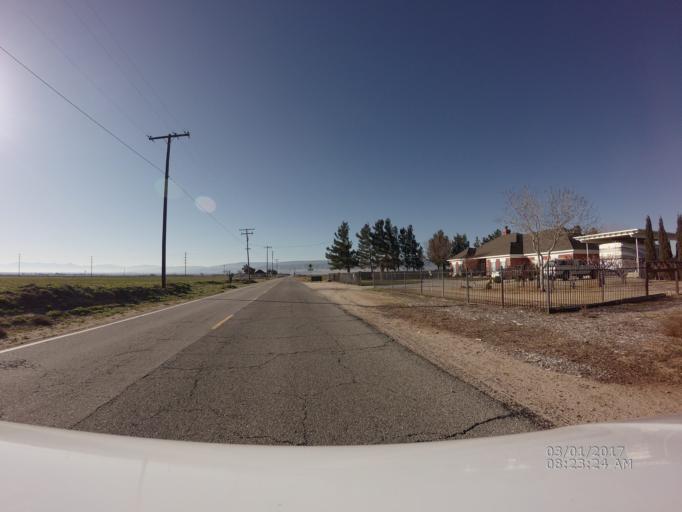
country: US
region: California
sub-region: Los Angeles County
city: Quartz Hill
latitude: 34.7204
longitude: -118.2546
